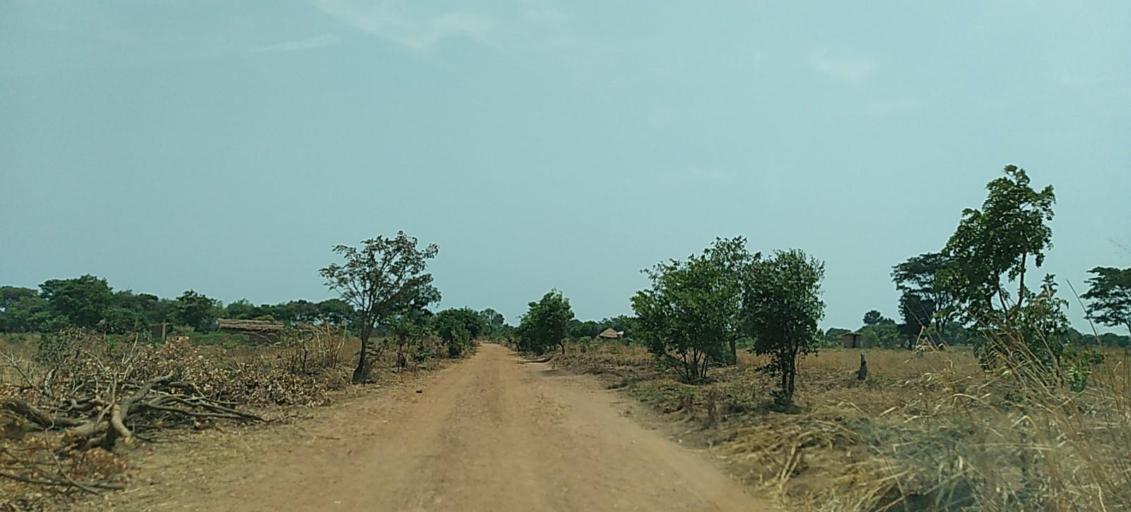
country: ZM
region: Copperbelt
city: Ndola
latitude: -13.0472
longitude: 28.7376
